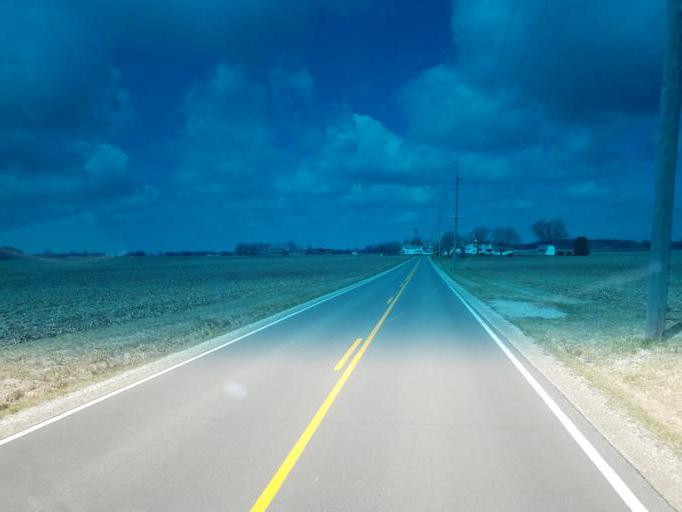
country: US
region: Ohio
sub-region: Crawford County
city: Bucyrus
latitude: 40.7871
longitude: -82.9127
